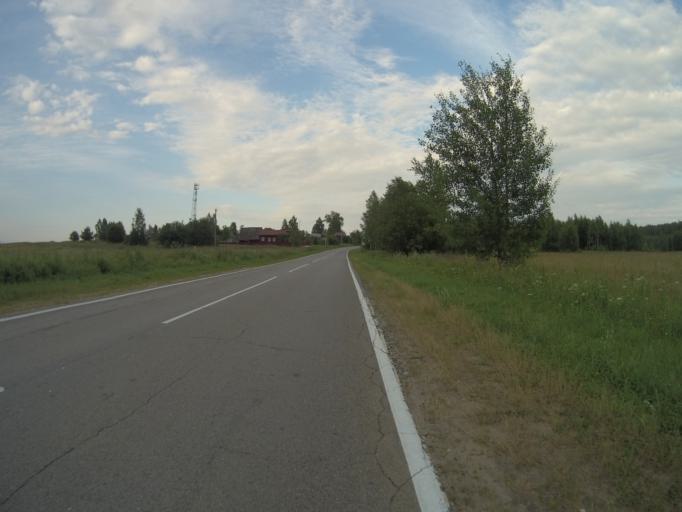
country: RU
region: Vladimir
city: Kameshkovo
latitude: 56.4058
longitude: 40.7872
